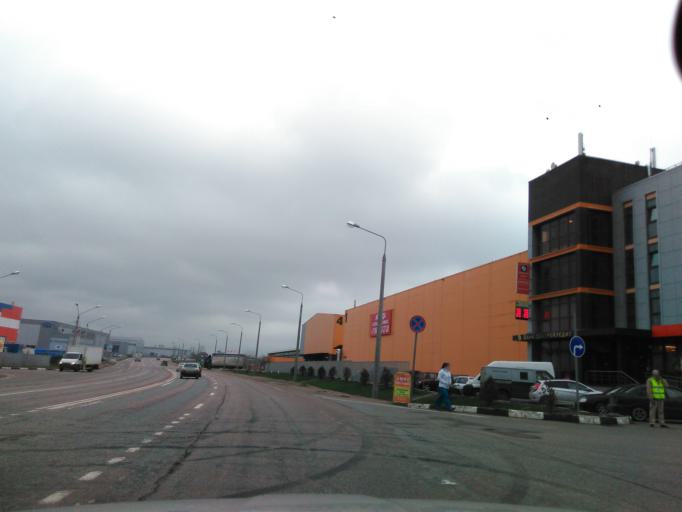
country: RU
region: Moskovskaya
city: Pavlovskaya Sloboda
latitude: 55.8160
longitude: 37.1143
